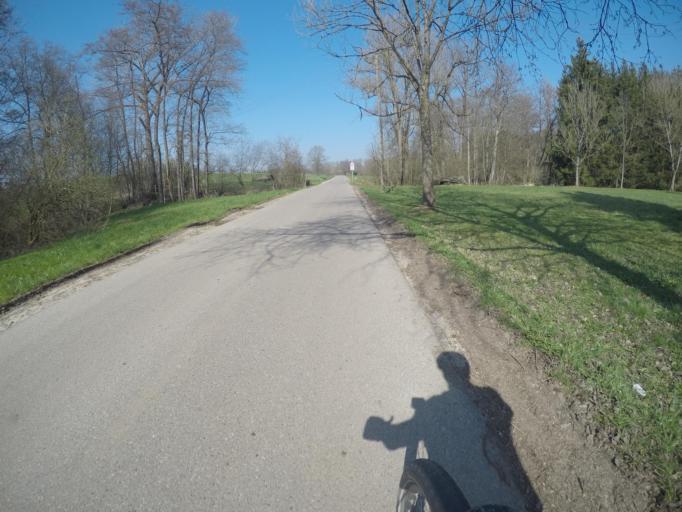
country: DE
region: Baden-Wuerttemberg
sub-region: Tuebingen Region
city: Pliezhausen
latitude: 48.5739
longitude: 9.2077
